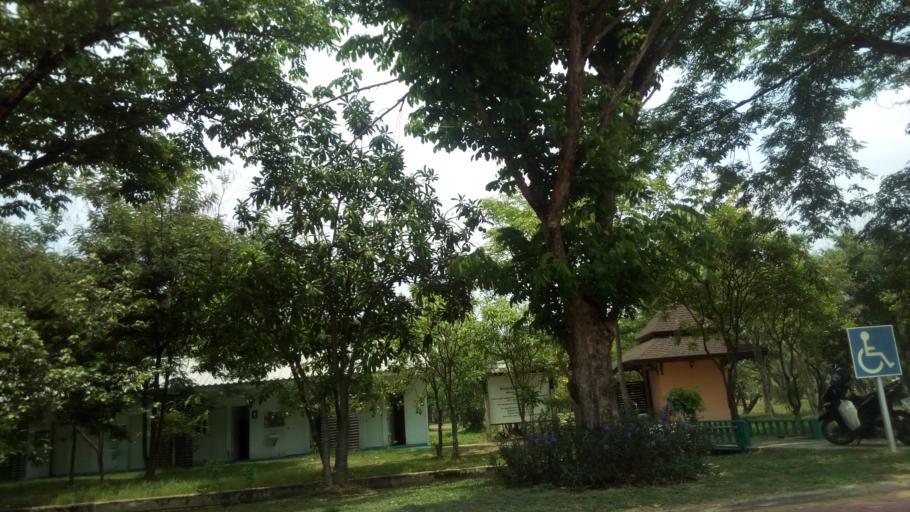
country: TH
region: Bangkok
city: Thawi Watthana
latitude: 13.7724
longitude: 100.3249
